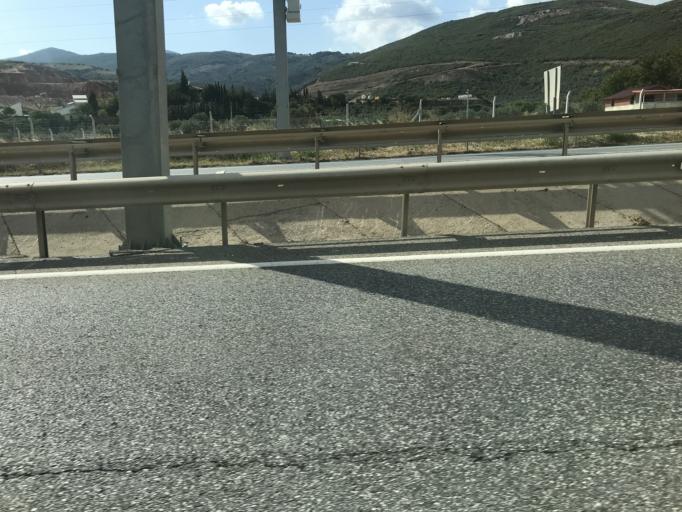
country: TR
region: Bursa
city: Orhangazi
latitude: 40.4721
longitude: 29.3006
